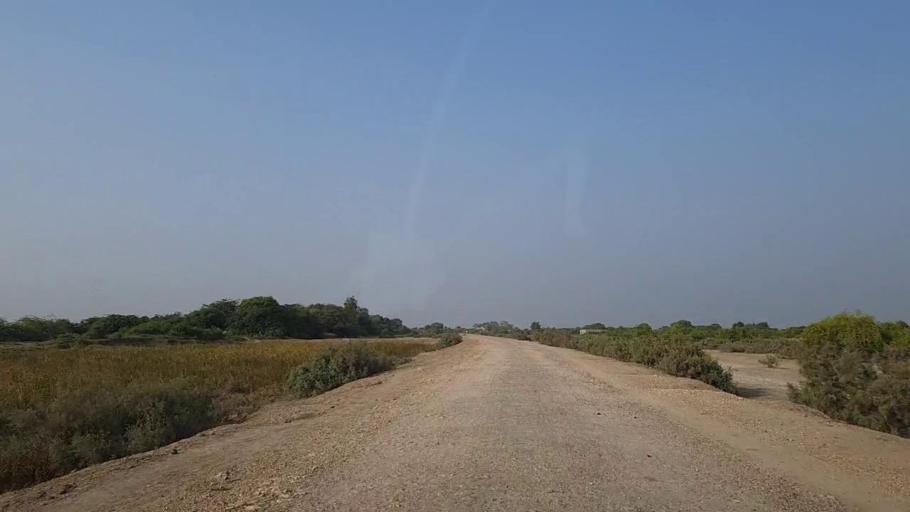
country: PK
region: Sindh
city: Mirpur Sakro
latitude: 24.6421
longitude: 67.7676
